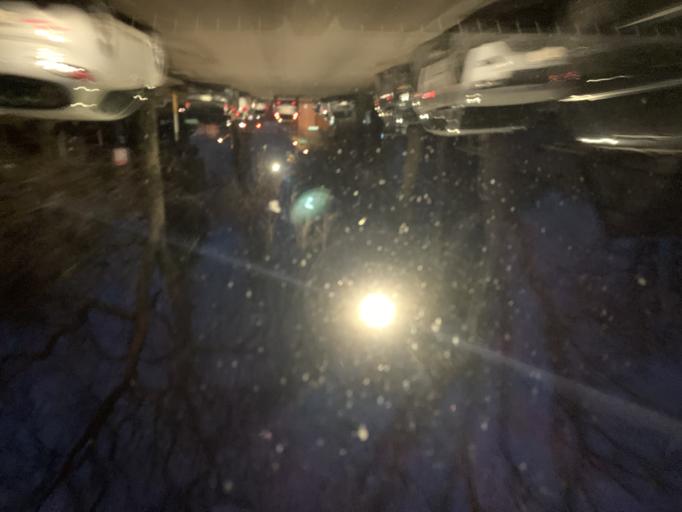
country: US
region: Colorado
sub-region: Jefferson County
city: Edgewater
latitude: 39.7706
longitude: -105.0486
